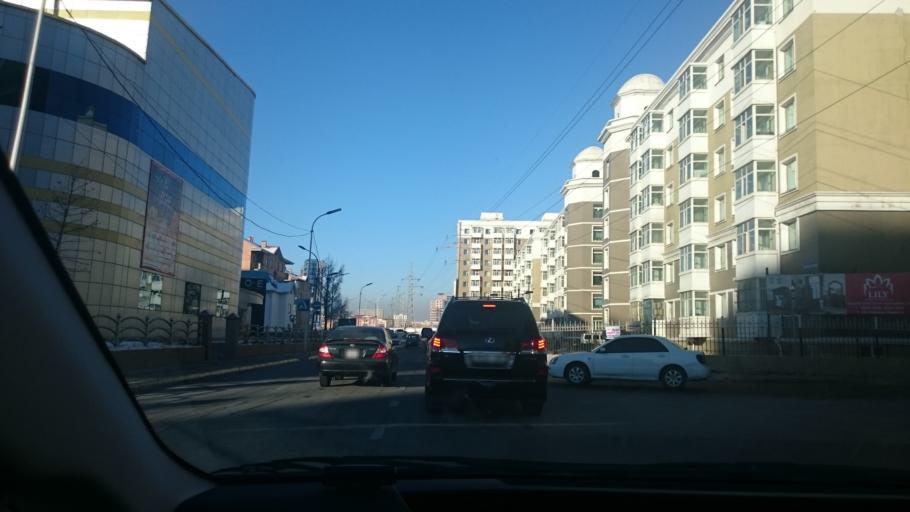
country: MN
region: Ulaanbaatar
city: Ulaanbaatar
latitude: 47.9041
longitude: 106.9282
